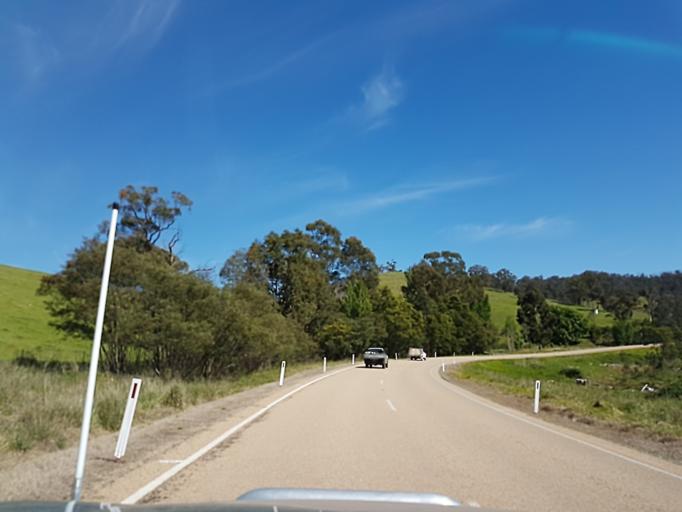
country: AU
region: Victoria
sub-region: East Gippsland
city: Bairnsdale
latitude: -37.4967
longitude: 147.8354
